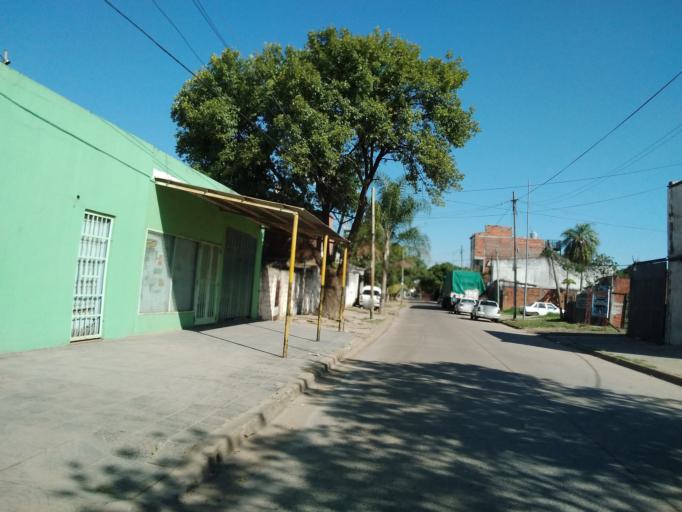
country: AR
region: Corrientes
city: Corrientes
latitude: -27.4845
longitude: -58.8081
